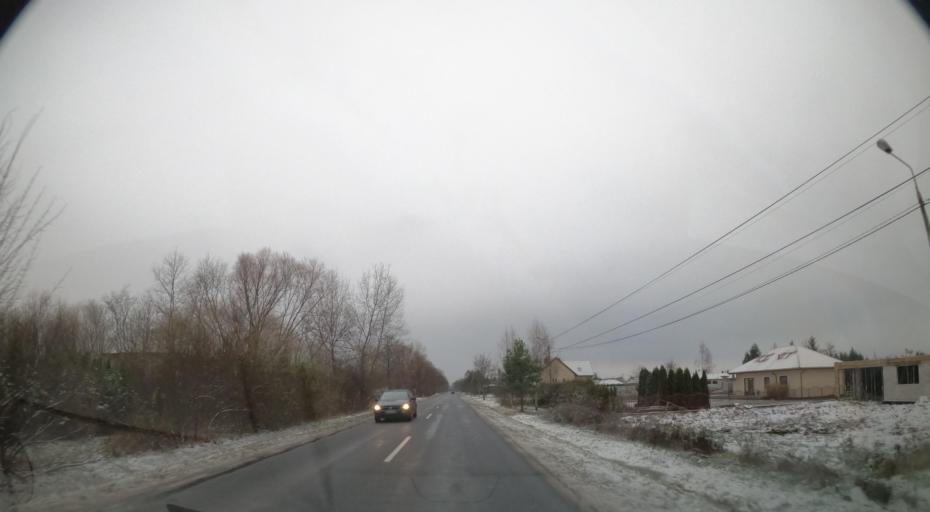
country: PL
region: Masovian Voivodeship
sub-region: Powiat plocki
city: Maszewo Duze
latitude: 52.5714
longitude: 19.6020
